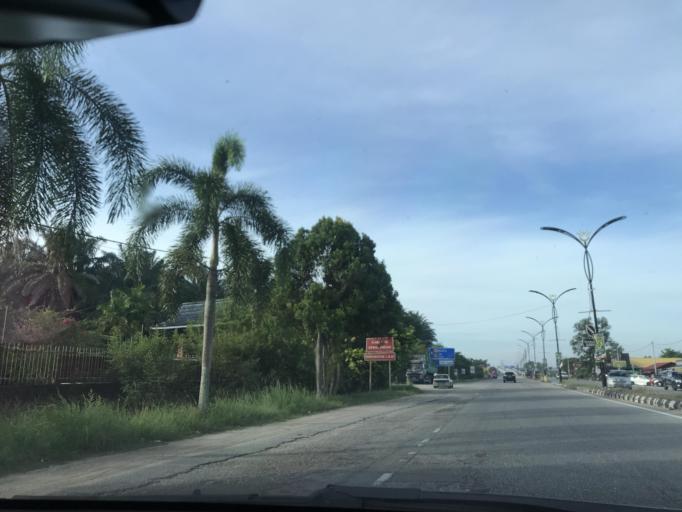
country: MY
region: Kelantan
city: Tanah Merah
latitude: 5.8175
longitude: 102.1485
